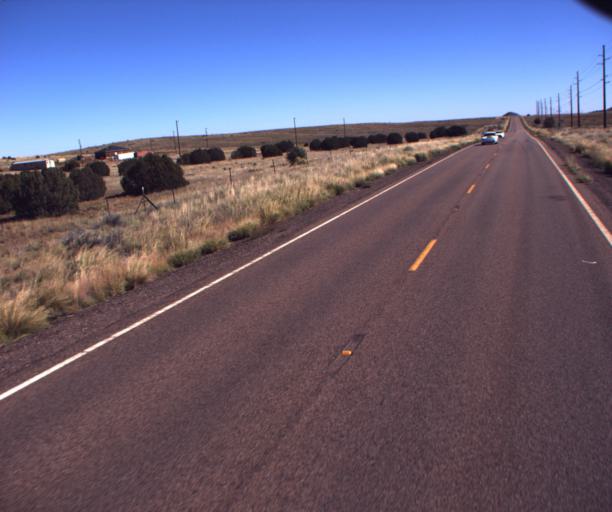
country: US
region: Arizona
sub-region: Navajo County
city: Taylor
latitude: 34.4871
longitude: -110.2398
